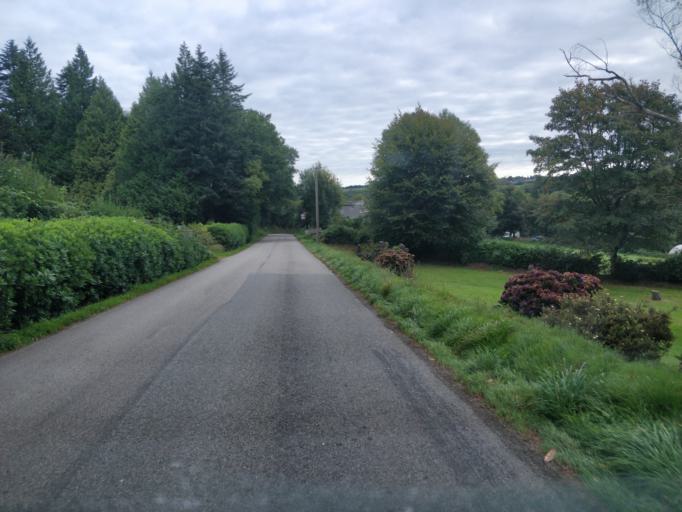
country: FR
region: Brittany
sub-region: Departement du Finistere
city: Plouneour-Menez
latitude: 48.4443
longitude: -3.8437
